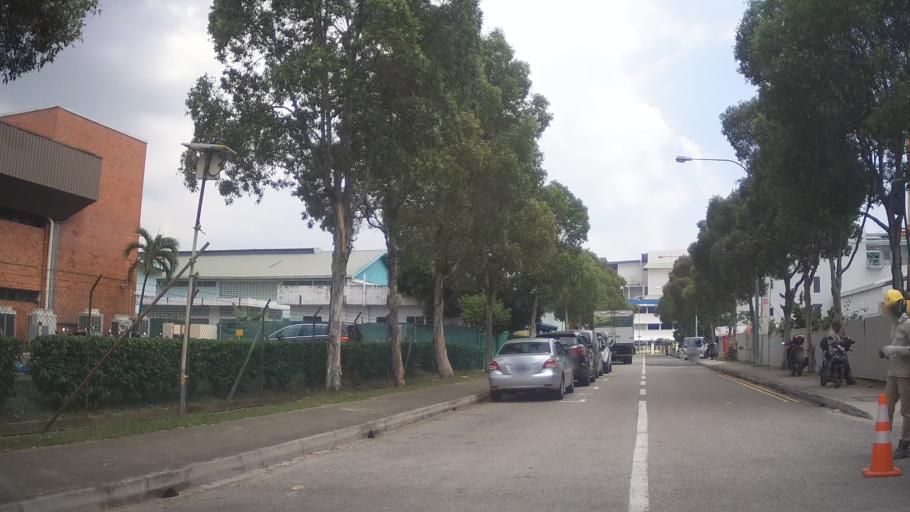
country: MY
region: Johor
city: Johor Bahru
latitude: 1.3171
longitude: 103.6634
